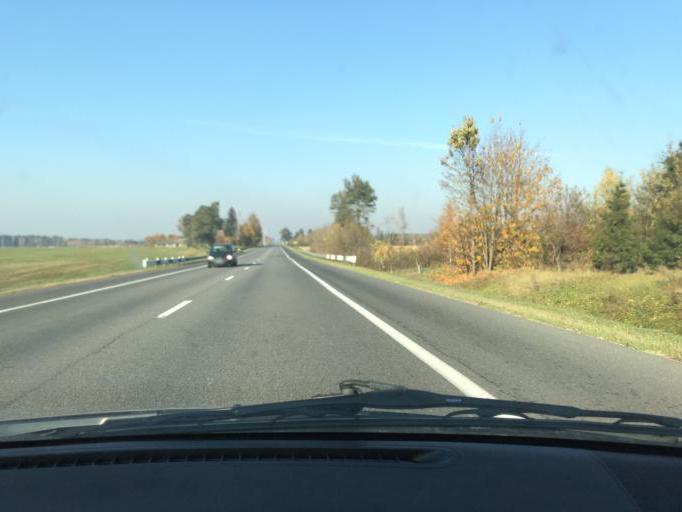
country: BY
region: Vitebsk
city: Orsha
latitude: 54.3711
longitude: 30.4444
